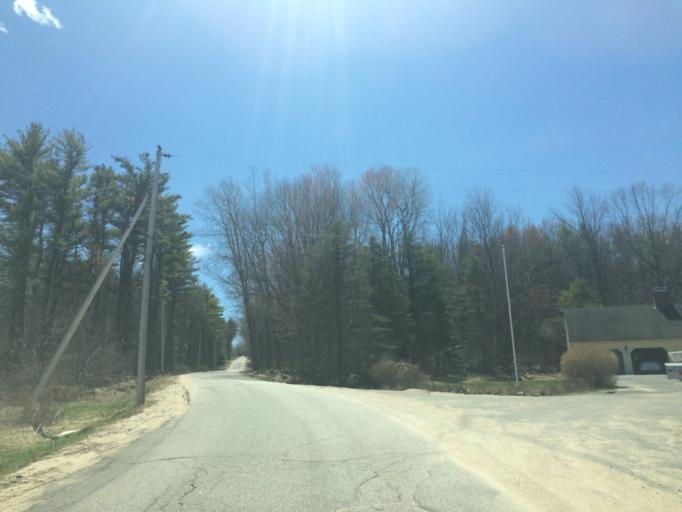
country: US
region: Maine
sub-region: Oxford County
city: Porter
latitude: 43.8006
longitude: -70.8764
